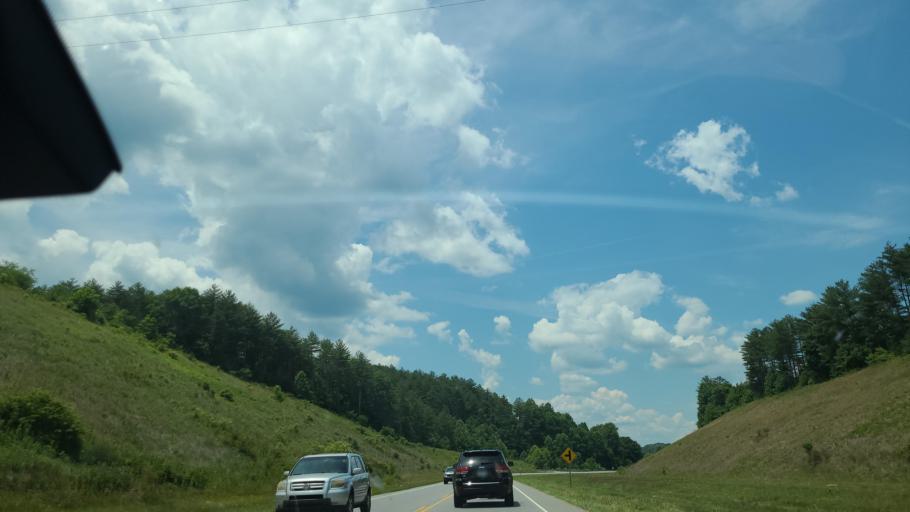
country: US
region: North Carolina
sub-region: Cherokee County
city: Murphy
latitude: 35.0734
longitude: -84.0218
